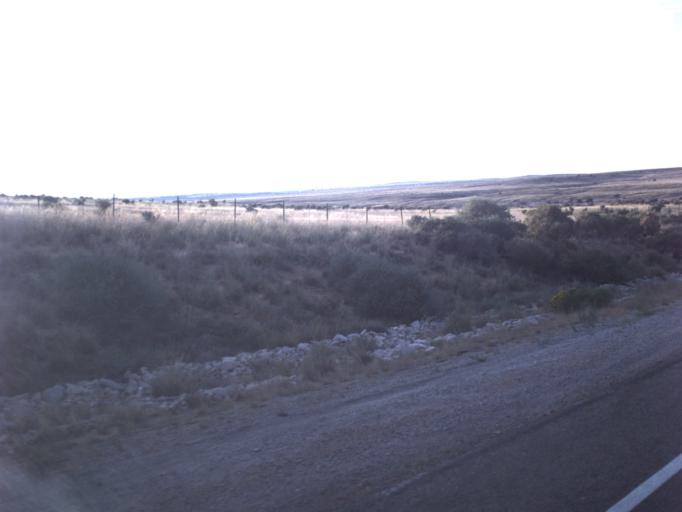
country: US
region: Utah
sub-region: San Juan County
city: Monticello
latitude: 38.2216
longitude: -109.3745
